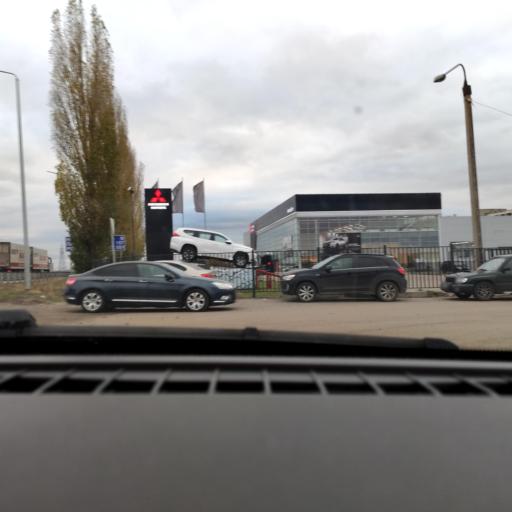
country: RU
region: Voronezj
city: Somovo
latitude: 51.6735
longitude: 39.3005
